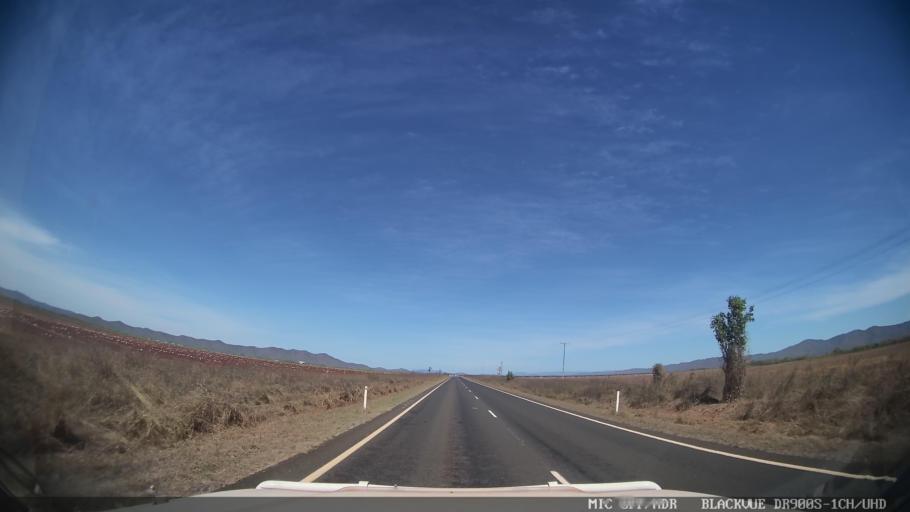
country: AU
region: Queensland
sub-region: Cook
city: Cooktown
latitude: -15.7939
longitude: 144.7113
